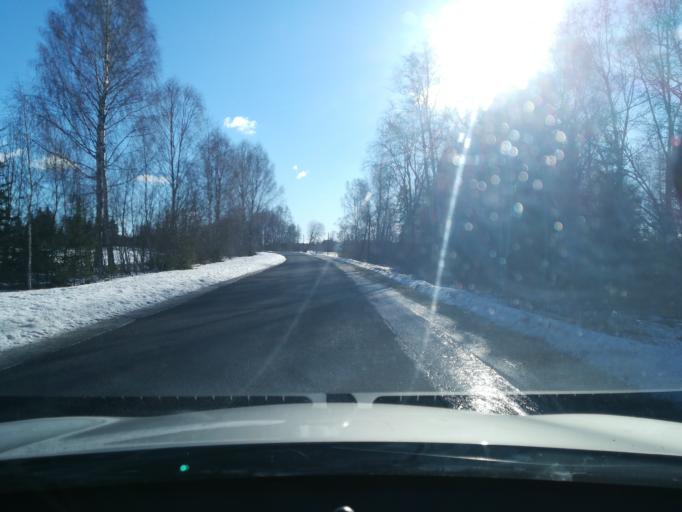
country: EE
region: Raplamaa
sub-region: Kohila vald
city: Kohila
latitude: 59.2404
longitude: 24.7520
